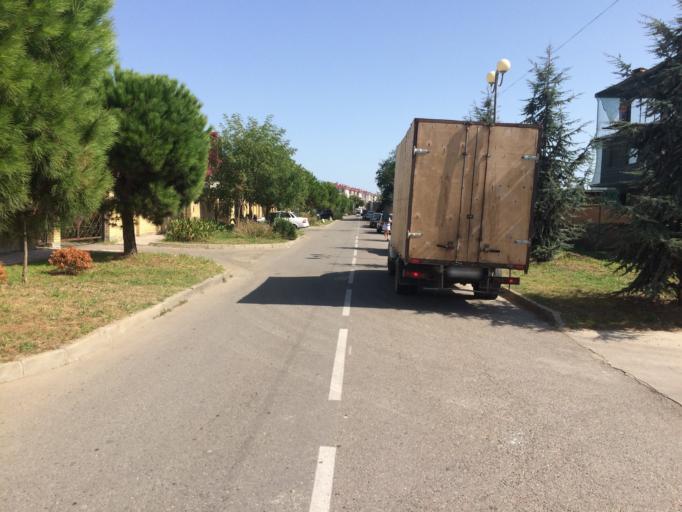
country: RU
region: Krasnodarskiy
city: Adler
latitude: 43.3983
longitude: 39.9697
